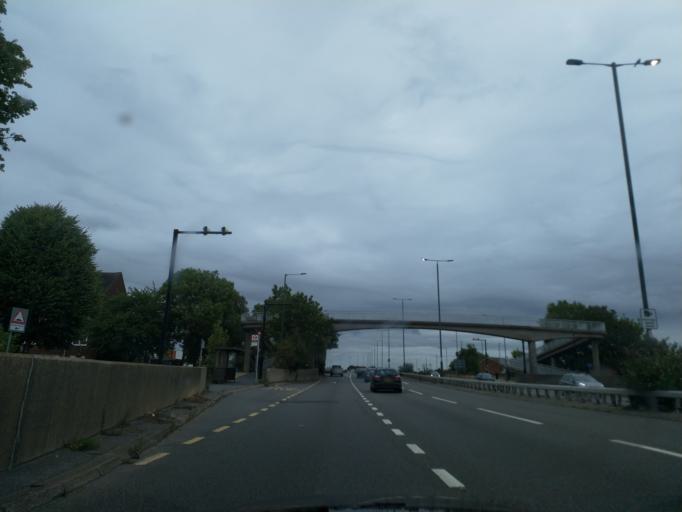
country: GB
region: England
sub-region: Greater London
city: Hampton
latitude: 51.4352
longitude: -0.3858
